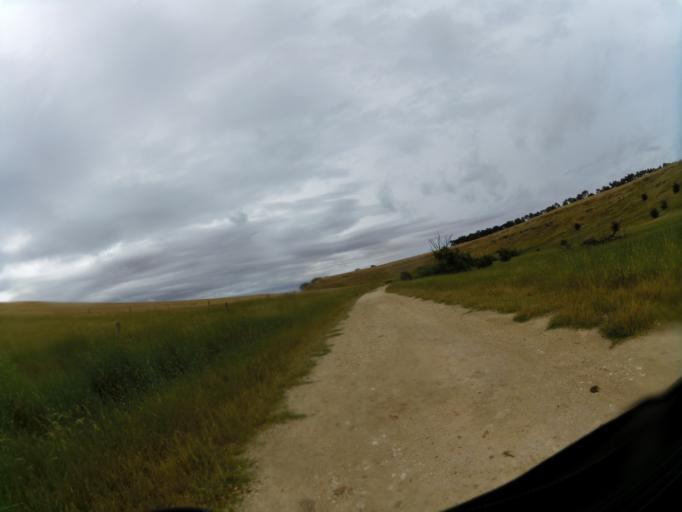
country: AU
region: Victoria
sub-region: Mount Alexander
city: Castlemaine
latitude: -37.2065
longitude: 144.0239
